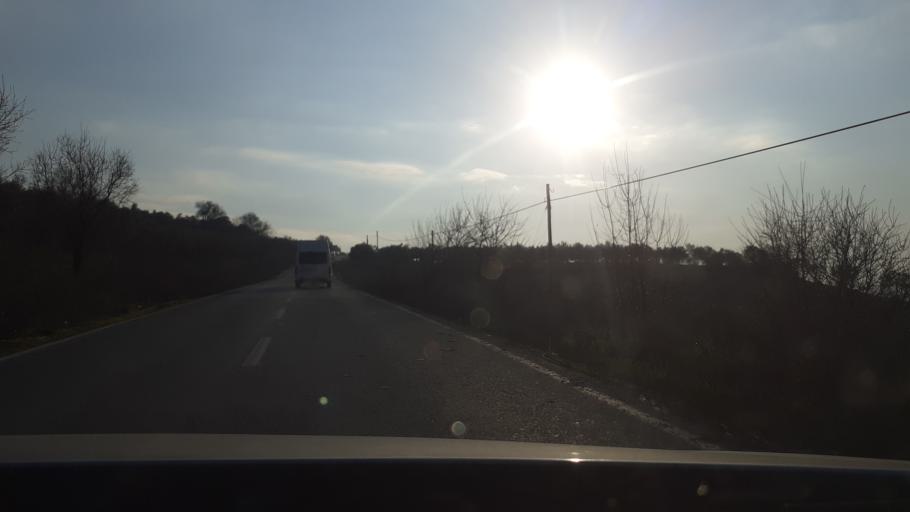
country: TR
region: Hatay
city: Oymakli
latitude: 36.1243
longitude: 36.3086
